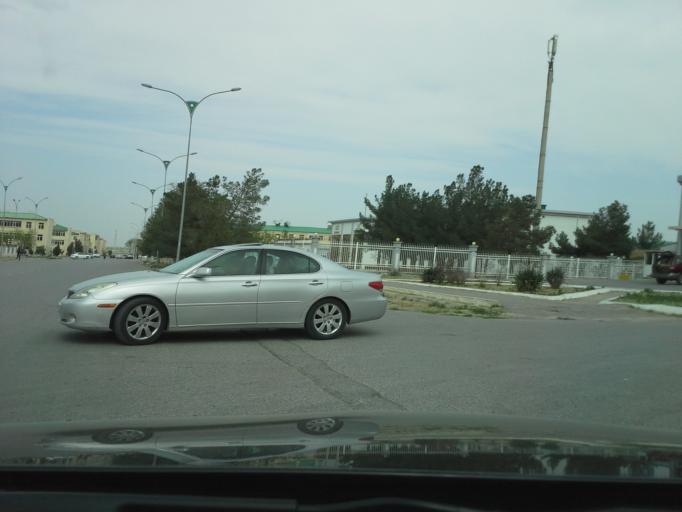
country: TM
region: Ahal
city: Abadan
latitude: 38.0566
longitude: 58.1498
